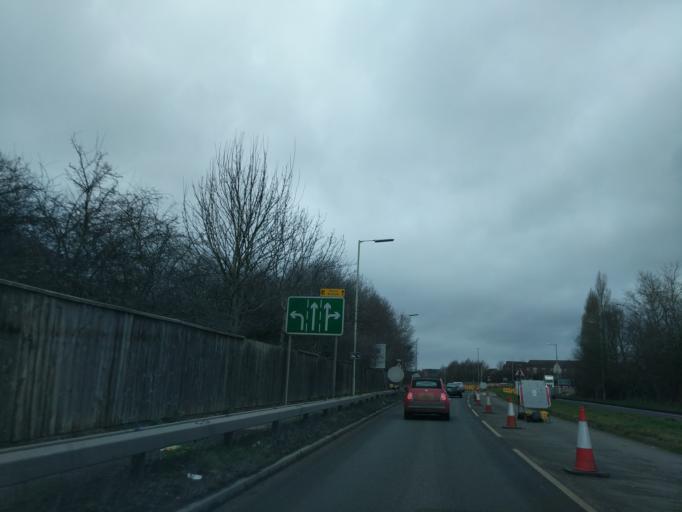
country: GB
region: England
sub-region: Staffordshire
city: Cannock
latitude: 52.6848
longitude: -2.0154
